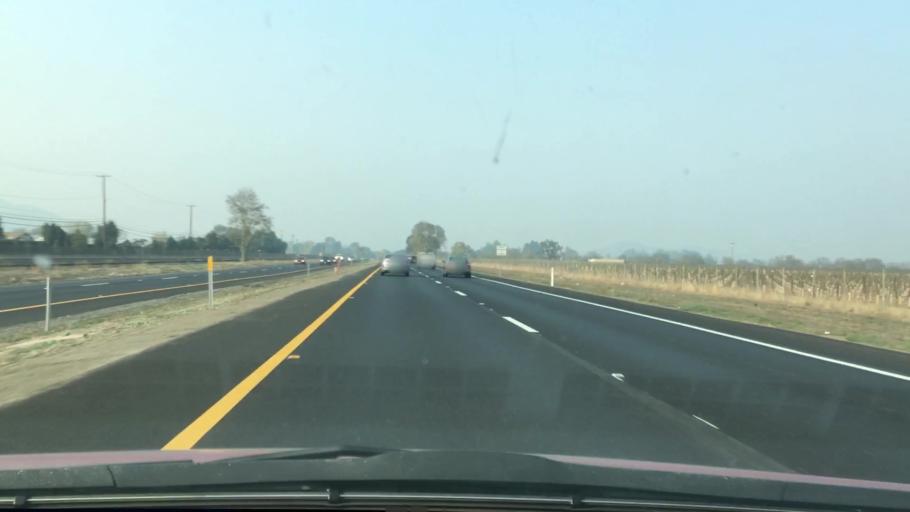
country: US
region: California
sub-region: Napa County
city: Yountville
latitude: 38.3476
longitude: -122.3285
